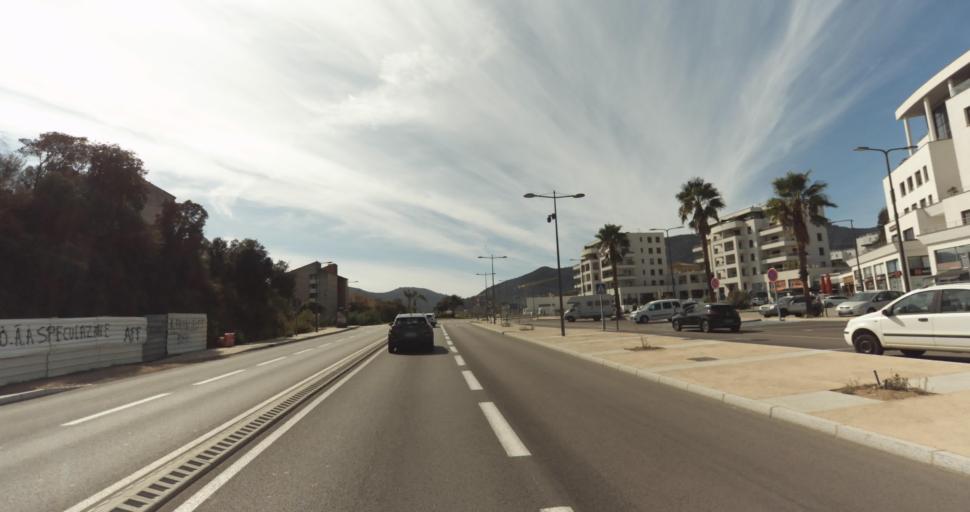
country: FR
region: Corsica
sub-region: Departement de la Corse-du-Sud
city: Ajaccio
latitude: 41.9424
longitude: 8.7510
